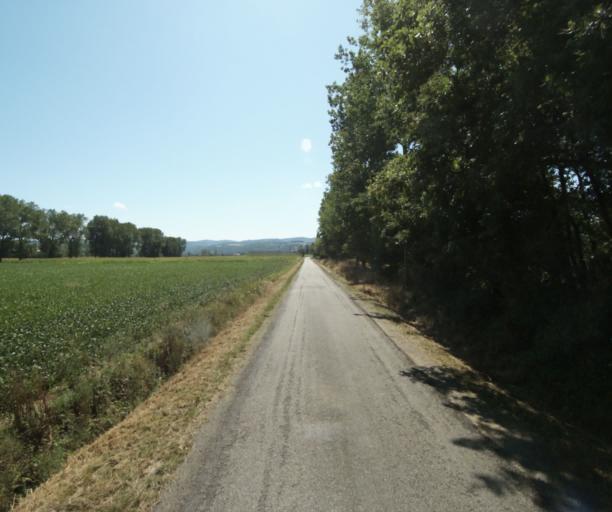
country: FR
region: Midi-Pyrenees
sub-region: Departement de la Haute-Garonne
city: Revel
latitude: 43.4647
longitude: 1.9657
